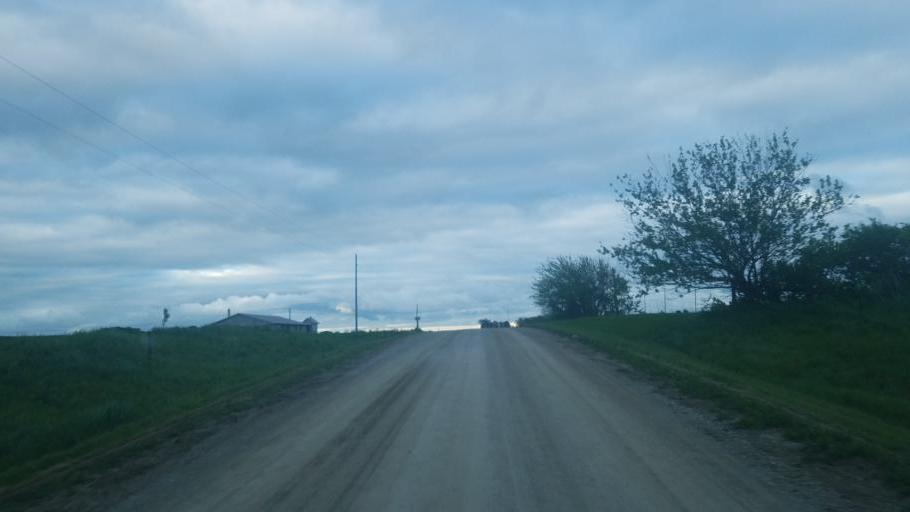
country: US
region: Iowa
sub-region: Decatur County
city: Lamoni
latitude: 40.5947
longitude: -93.9573
